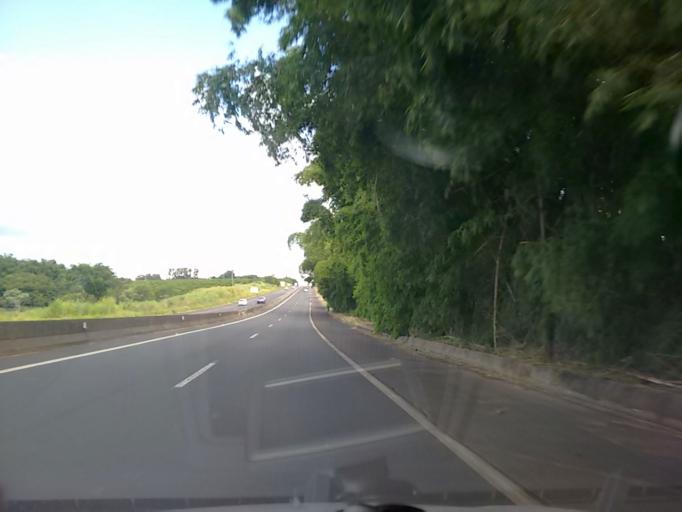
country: BR
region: Sao Paulo
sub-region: Marilia
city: Marilia
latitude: -22.2183
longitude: -49.8371
